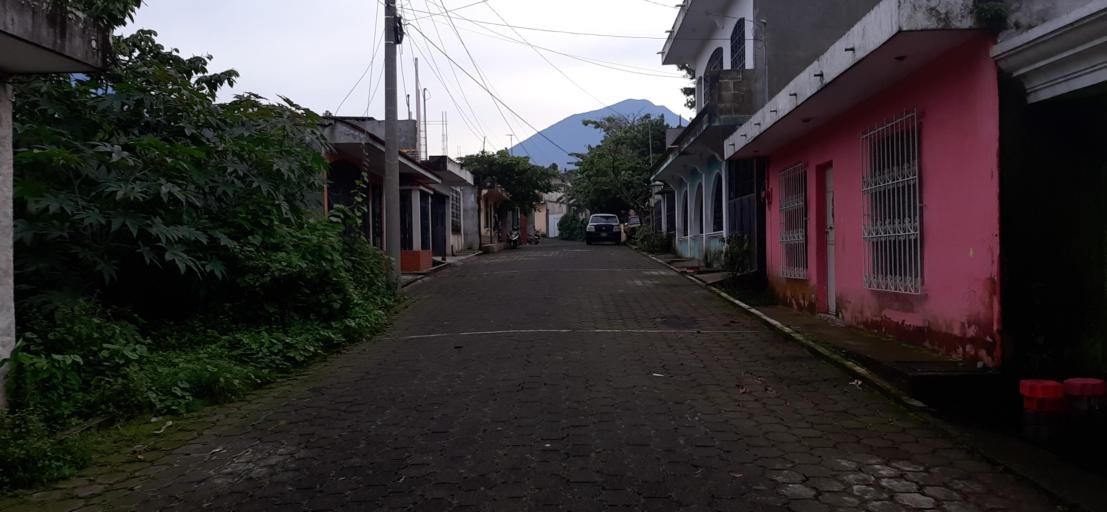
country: GT
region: Retalhuleu
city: San Felipe
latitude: 14.6212
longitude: -91.5984
